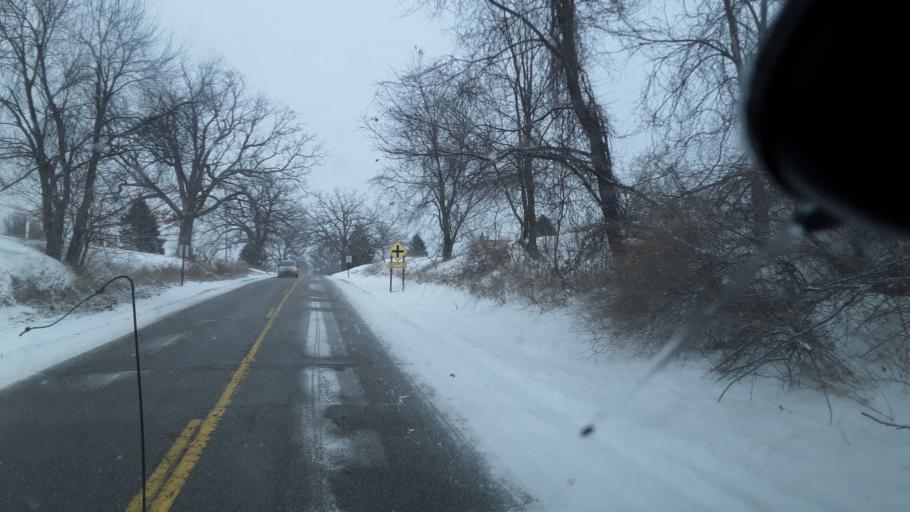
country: US
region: Michigan
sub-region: Ingham County
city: Leslie
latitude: 42.4896
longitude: -84.3346
